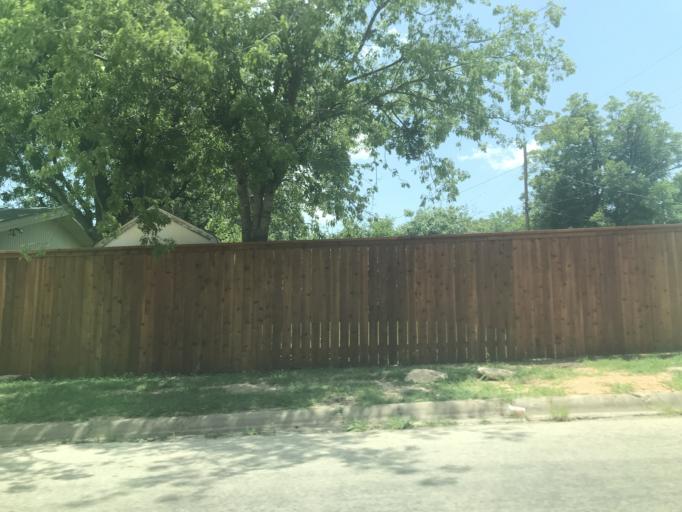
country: US
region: Texas
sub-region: Taylor County
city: Abilene
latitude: 32.4714
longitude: -99.7145
